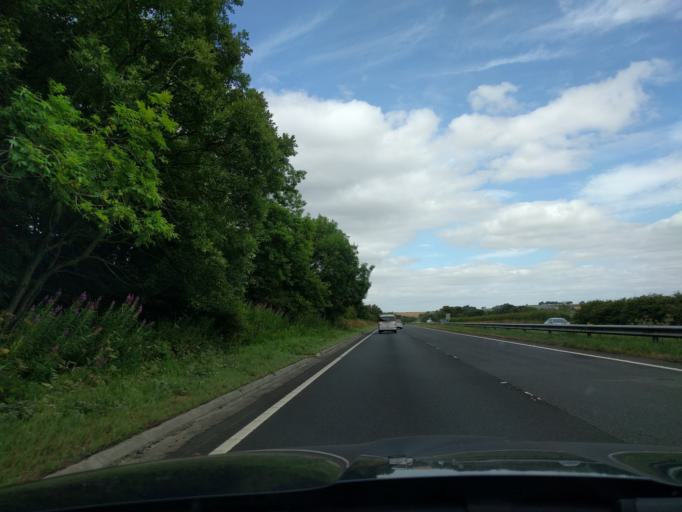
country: GB
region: England
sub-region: Northumberland
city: Felton
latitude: 55.3415
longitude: -1.7269
